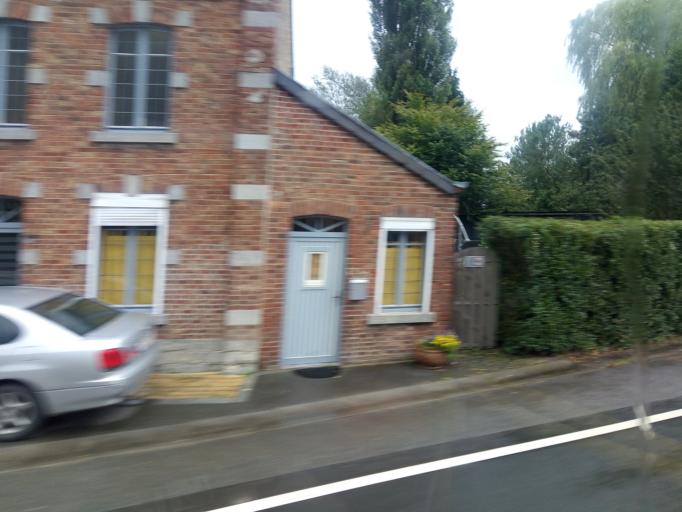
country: BE
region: Wallonia
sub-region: Province du Luxembourg
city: Hotton
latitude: 50.2562
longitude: 5.4761
